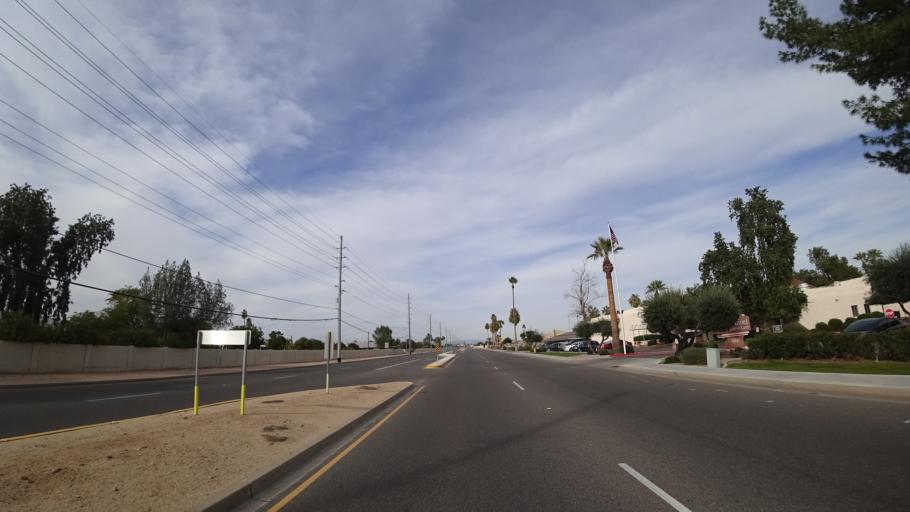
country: US
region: Arizona
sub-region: Maricopa County
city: Sun City
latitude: 33.5858
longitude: -112.2726
